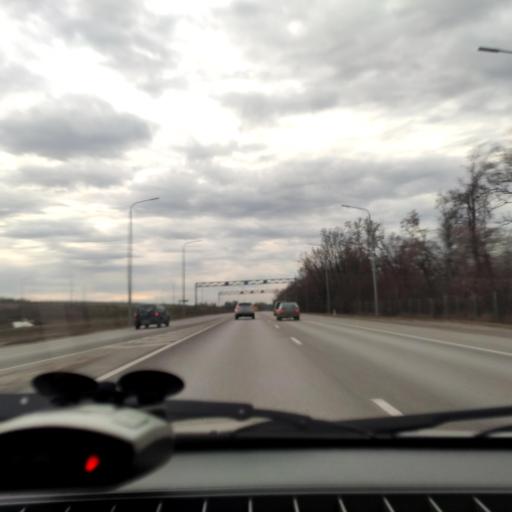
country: RU
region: Voronezj
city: Podgornoye
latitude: 51.8381
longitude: 39.2138
